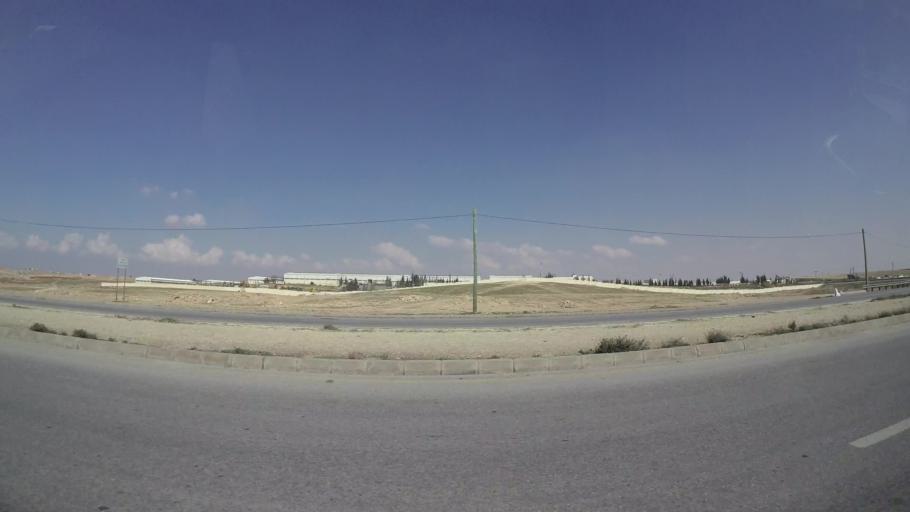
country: JO
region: Zarqa
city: Zarqa
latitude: 32.0540
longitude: 36.1312
